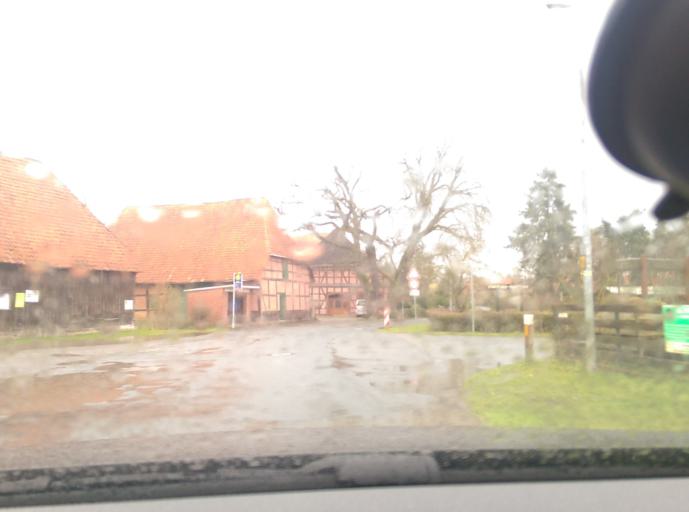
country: DE
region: Lower Saxony
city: Schwarmstedt
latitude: 52.6326
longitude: 9.6065
